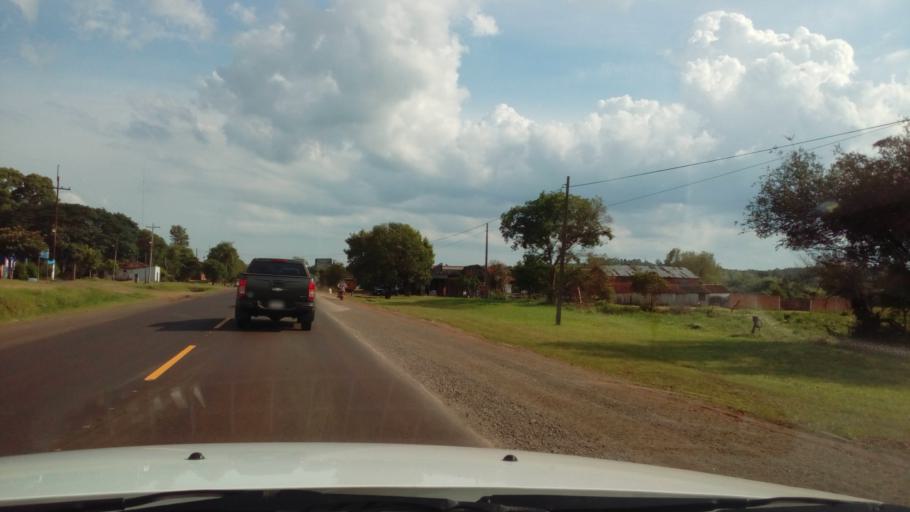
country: PY
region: Itapua
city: Capitan Miranda
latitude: -27.2633
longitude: -55.8175
